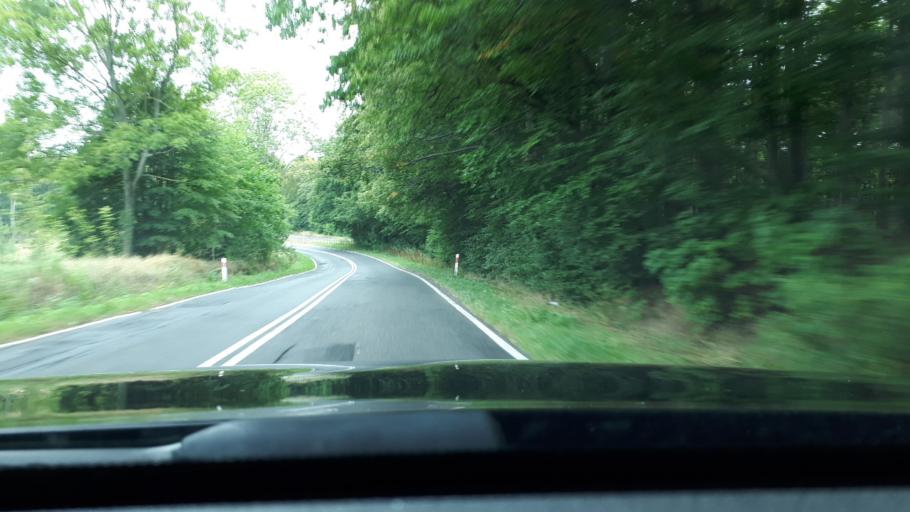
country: PL
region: Lower Silesian Voivodeship
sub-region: Powiat lwowecki
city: Gryfow Slaski
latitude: 51.0830
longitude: 15.4711
